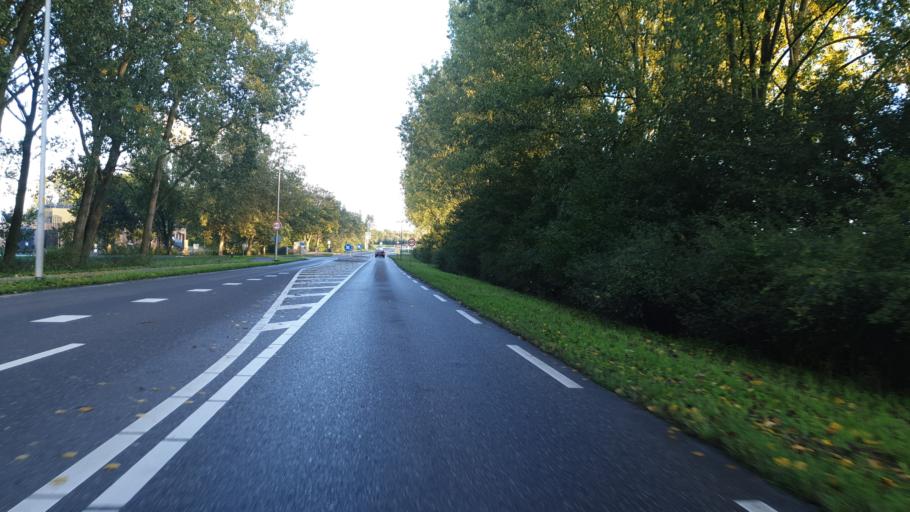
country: NL
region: Gelderland
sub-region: Gemeente Druten
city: Druten
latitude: 51.8715
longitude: 5.6109
